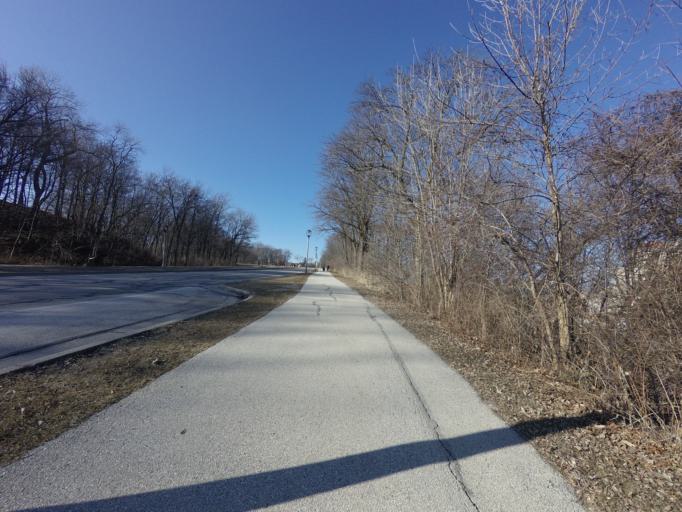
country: US
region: Wisconsin
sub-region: Milwaukee County
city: Shorewood
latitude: 43.0712
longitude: -87.8671
